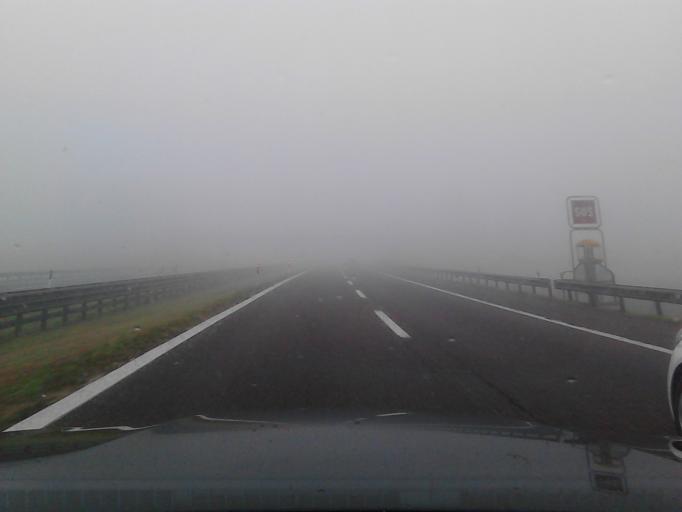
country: IT
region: Veneto
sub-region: Provincia di Verona
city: Nogarole Rocca
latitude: 45.3042
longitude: 10.9037
